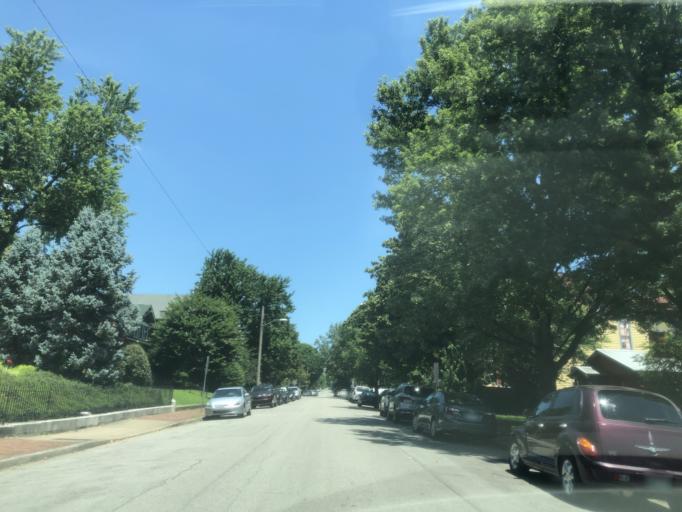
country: US
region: Tennessee
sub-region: Davidson County
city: Nashville
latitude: 36.1734
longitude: -86.7574
